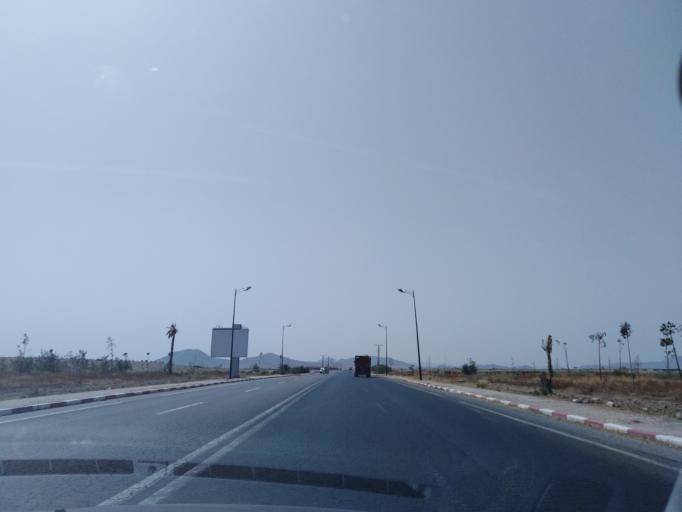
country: MA
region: Marrakech-Tensift-Al Haouz
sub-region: Marrakech
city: Marrakesh
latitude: 31.7664
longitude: -8.1207
